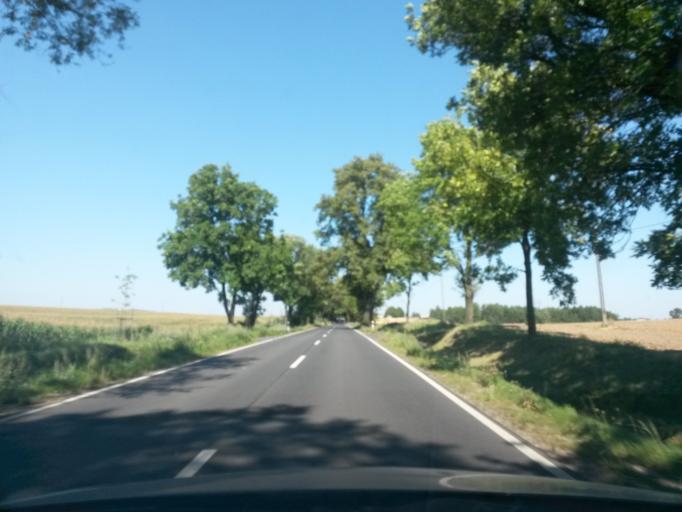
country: PL
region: Warmian-Masurian Voivodeship
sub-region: Powiat ilawski
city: Lubawa
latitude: 53.3992
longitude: 19.8038
